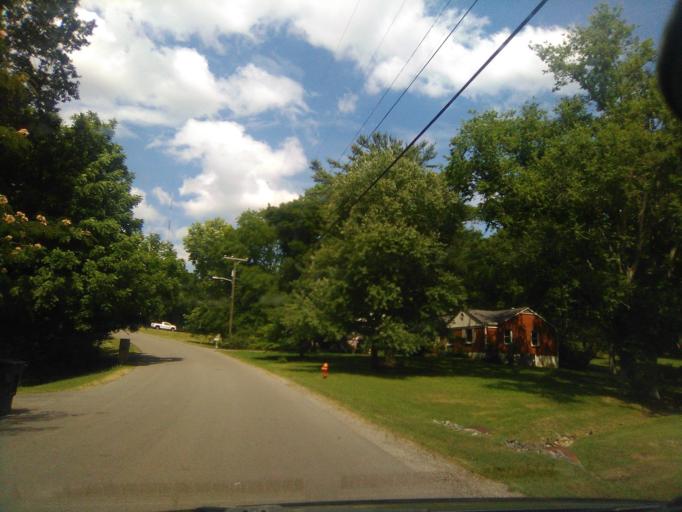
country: US
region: Tennessee
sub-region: Davidson County
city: Belle Meade
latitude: 36.1339
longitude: -86.8799
